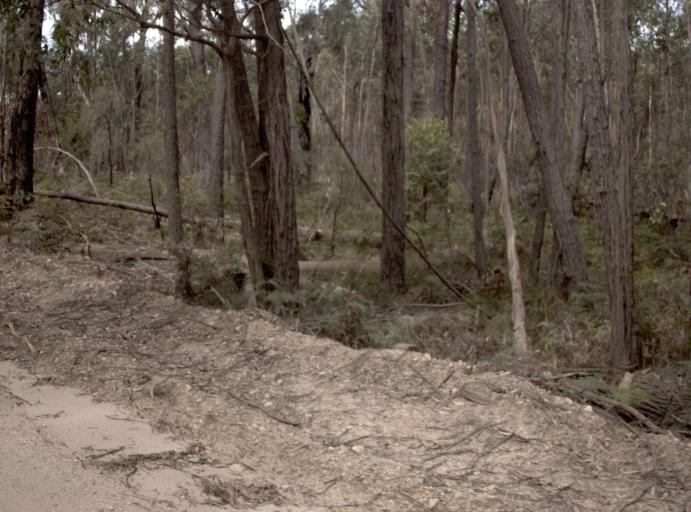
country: AU
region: Victoria
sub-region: East Gippsland
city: Lakes Entrance
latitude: -37.6816
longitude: 148.6241
